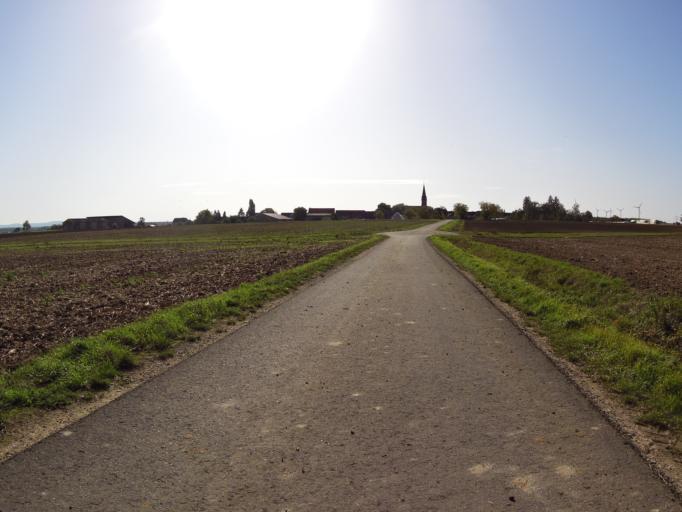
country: DE
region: Bavaria
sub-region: Regierungsbezirk Unterfranken
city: Biebelried
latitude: 49.7496
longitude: 10.0630
